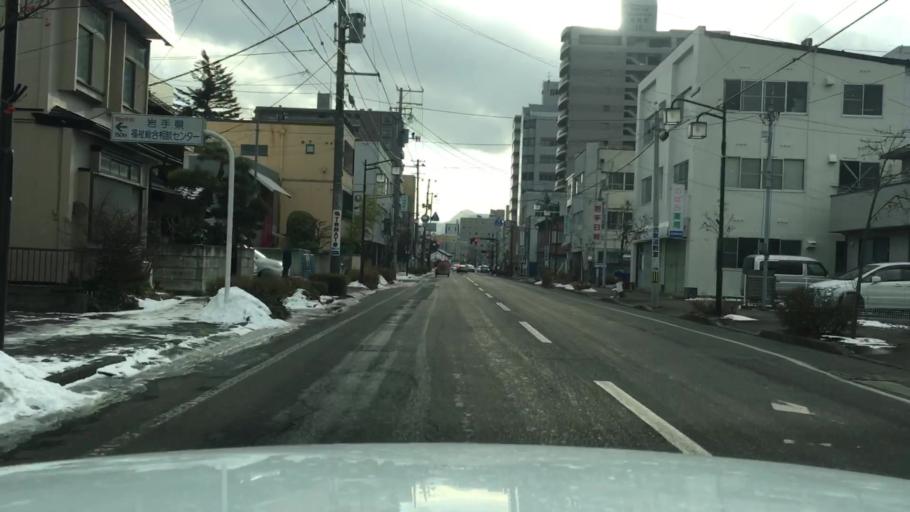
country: JP
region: Iwate
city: Morioka-shi
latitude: 39.7077
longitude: 141.1413
